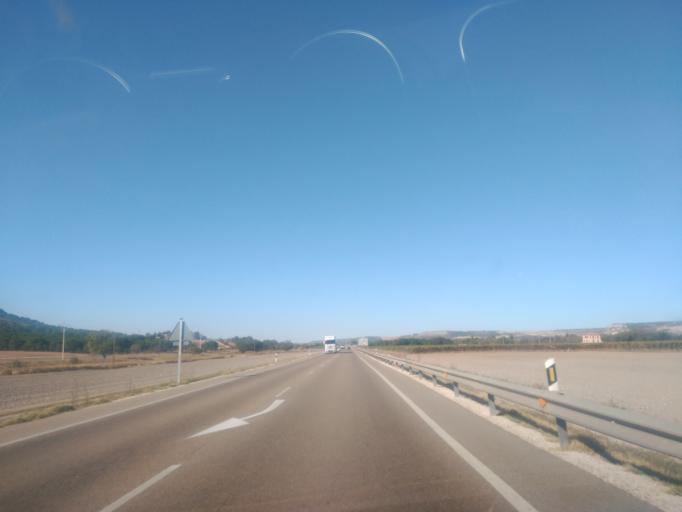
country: ES
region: Castille and Leon
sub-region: Provincia de Valladolid
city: Quintanilla de Onesimo
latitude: 41.6274
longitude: -4.3348
